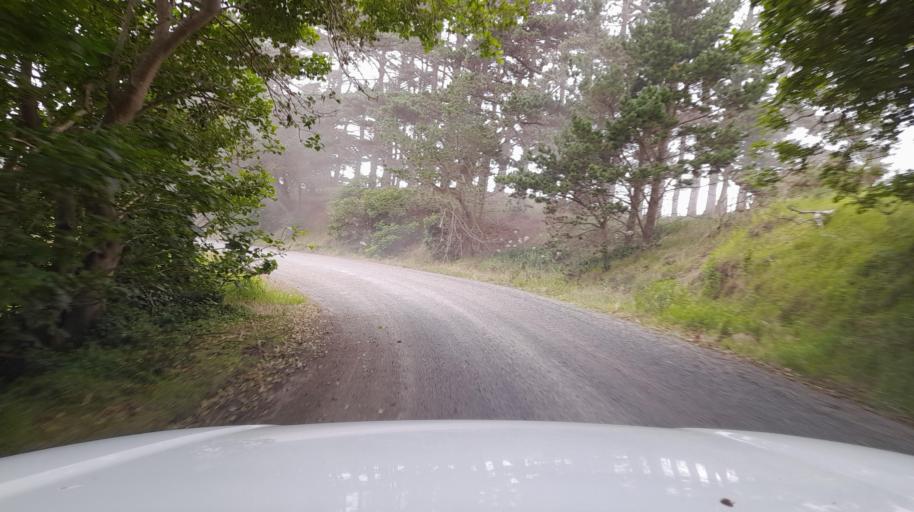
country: NZ
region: Northland
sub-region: Far North District
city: Ahipara
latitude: -35.1434
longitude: 173.1802
